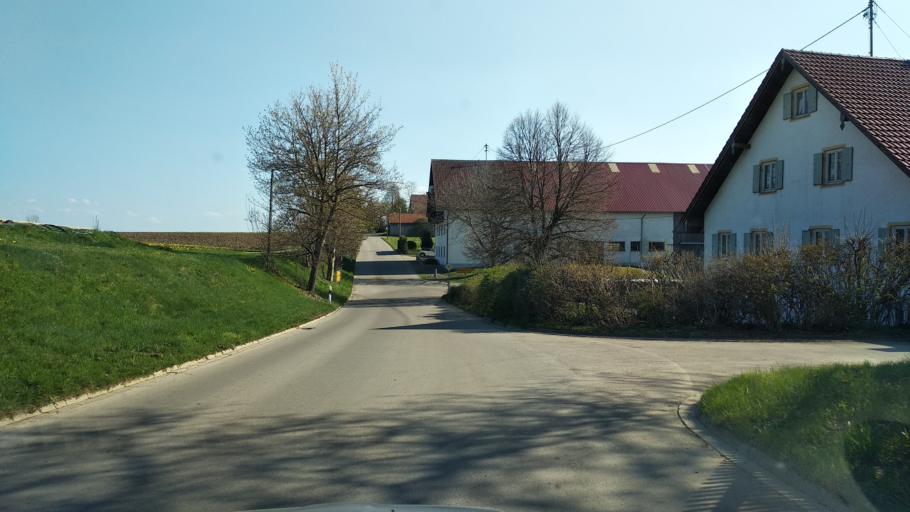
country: DE
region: Bavaria
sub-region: Swabia
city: Wald
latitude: 47.9816
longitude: 10.3101
